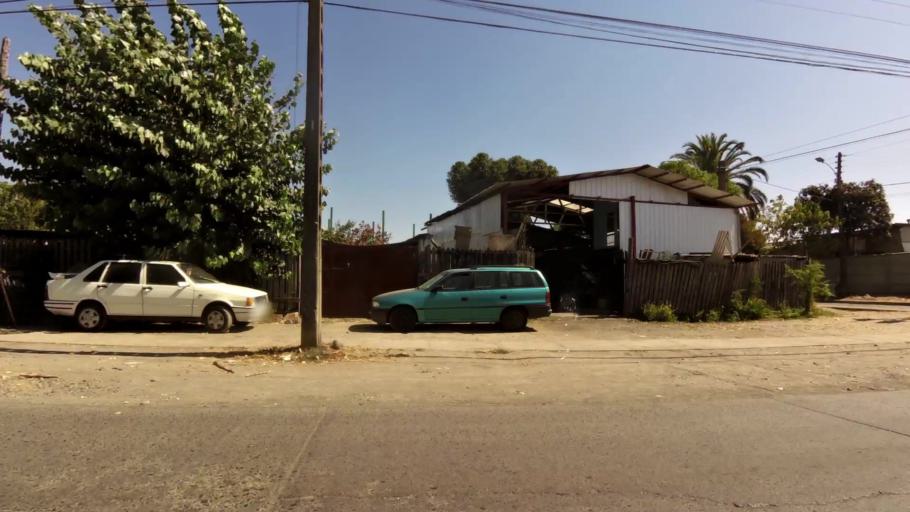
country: CL
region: Maule
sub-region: Provincia de Talca
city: Talca
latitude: -35.4417
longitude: -71.6629
